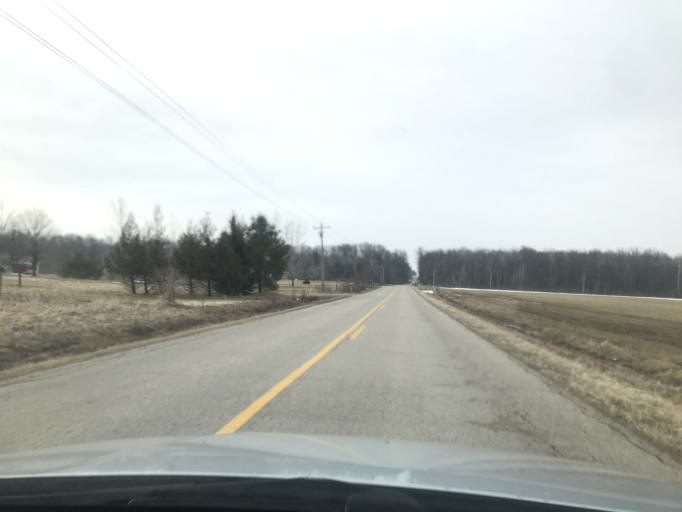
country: US
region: Wisconsin
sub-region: Oconto County
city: Oconto Falls
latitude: 44.8393
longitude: -88.1678
